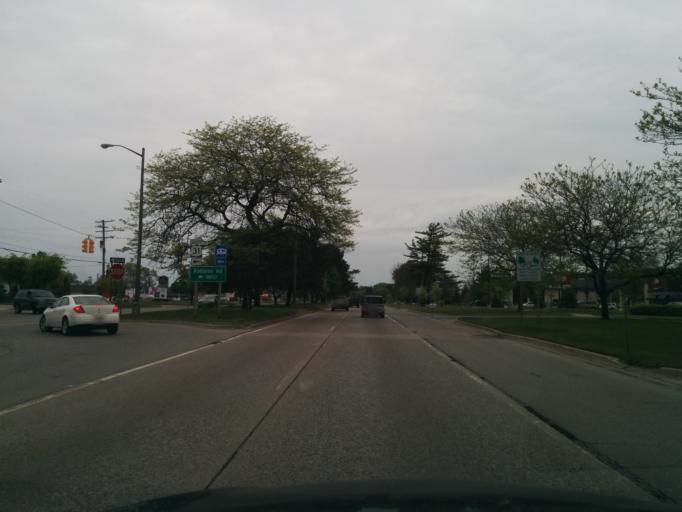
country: US
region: Michigan
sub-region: Ottawa County
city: Grand Haven
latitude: 43.0460
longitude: -86.2202
